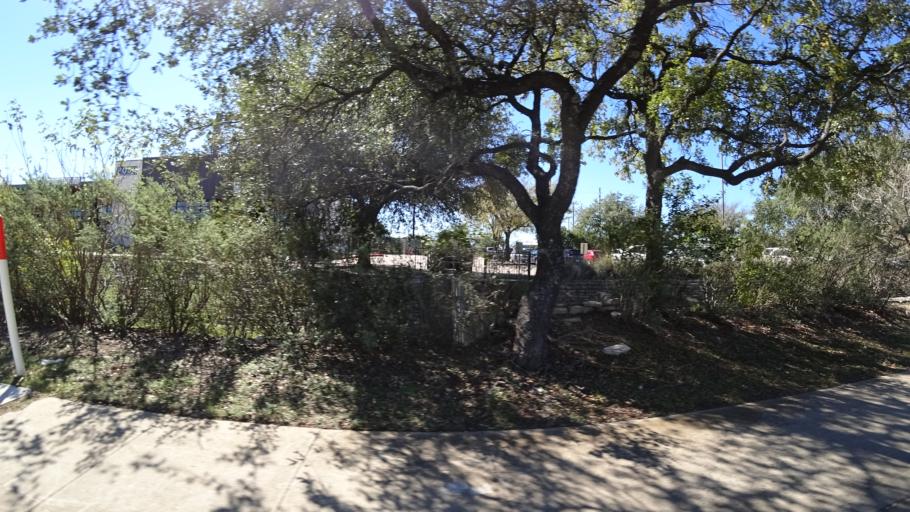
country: US
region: Texas
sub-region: Travis County
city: Rollingwood
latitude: 30.2330
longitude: -97.8117
